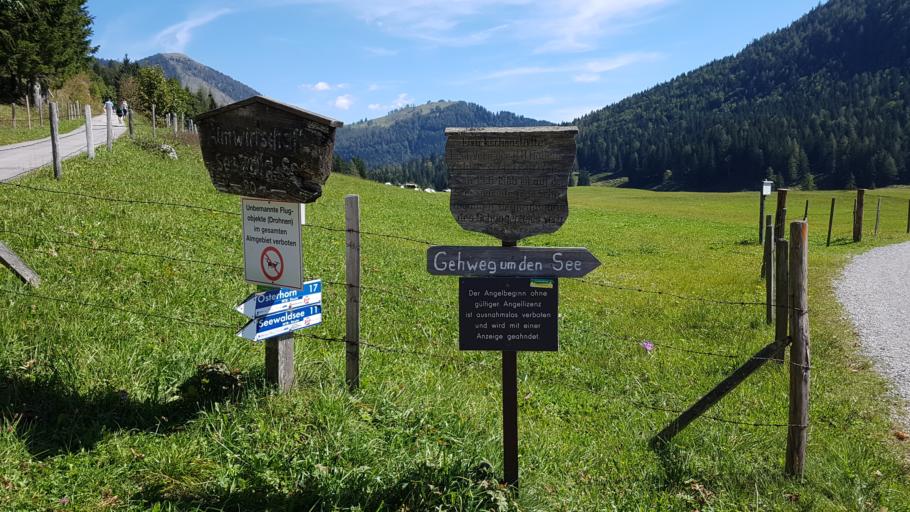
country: AT
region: Salzburg
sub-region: Politischer Bezirk Hallein
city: Scheffau am Tennengebirge
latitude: 47.6283
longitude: 13.2685
